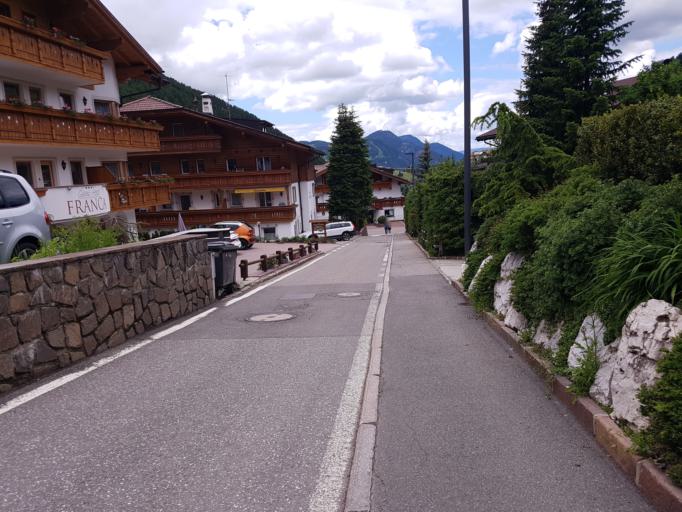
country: IT
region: Trentino-Alto Adige
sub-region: Bolzano
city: Selva
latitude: 46.5564
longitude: 11.7607
